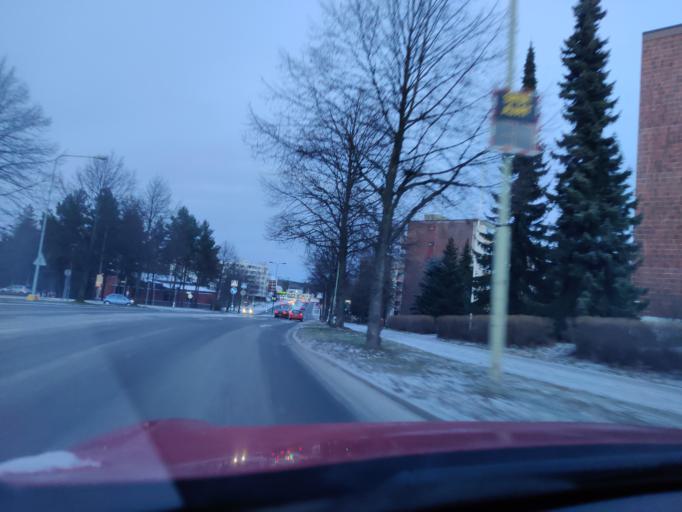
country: FI
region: Pirkanmaa
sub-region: Tampere
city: Nokia
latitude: 61.4780
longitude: 23.5144
